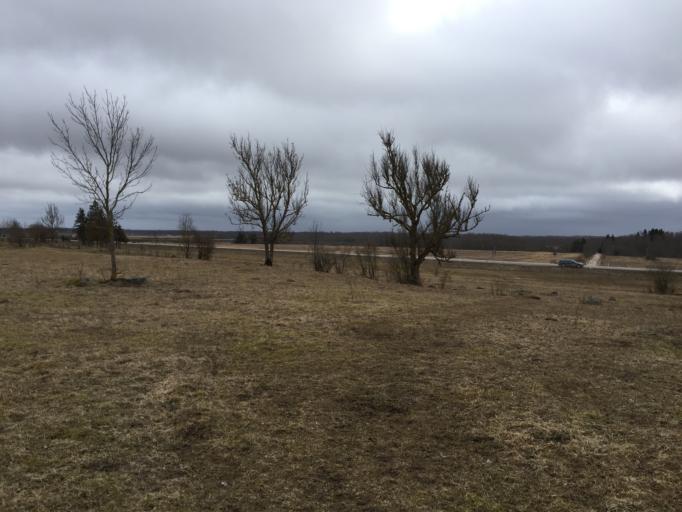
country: EE
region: Laeaene
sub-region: Lihula vald
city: Lihula
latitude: 58.7272
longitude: 23.9290
